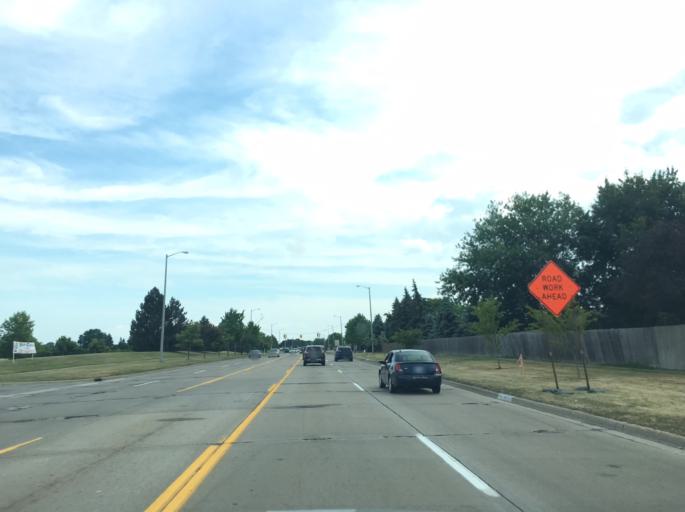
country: US
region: Michigan
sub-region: Macomb County
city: Fraser
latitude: 42.5625
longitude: -82.9878
